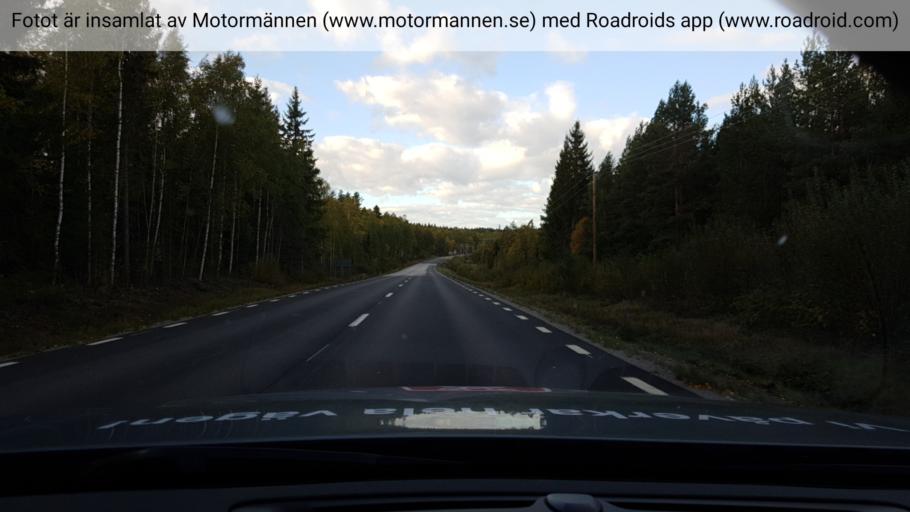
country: SE
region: Vaermland
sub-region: Filipstads Kommun
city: Lesjofors
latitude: 59.9217
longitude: 13.9819
